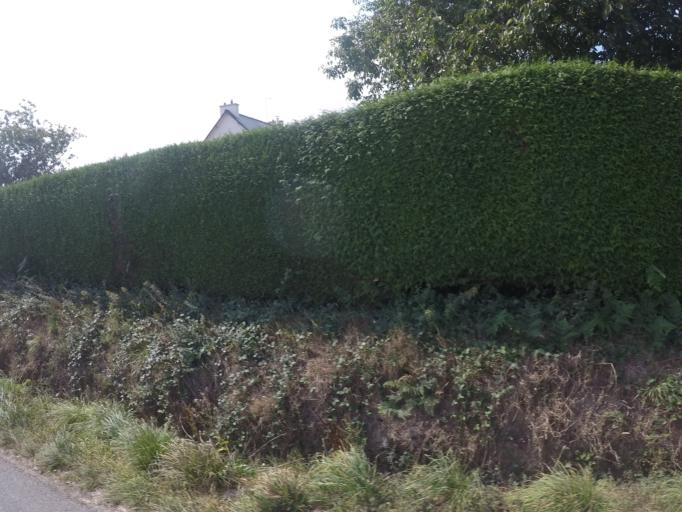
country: FR
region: Brittany
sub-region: Departement des Cotes-d'Armor
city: Tremuson
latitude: 48.5486
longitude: -2.8922
